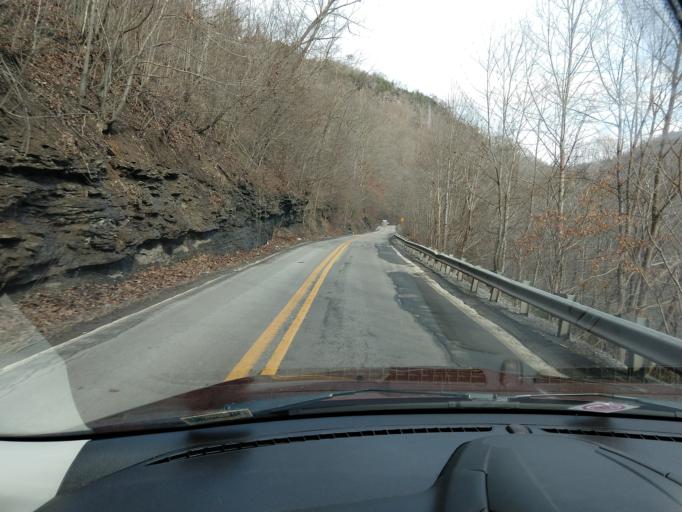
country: US
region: West Virginia
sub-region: McDowell County
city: Welch
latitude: 37.3203
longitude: -81.7034
